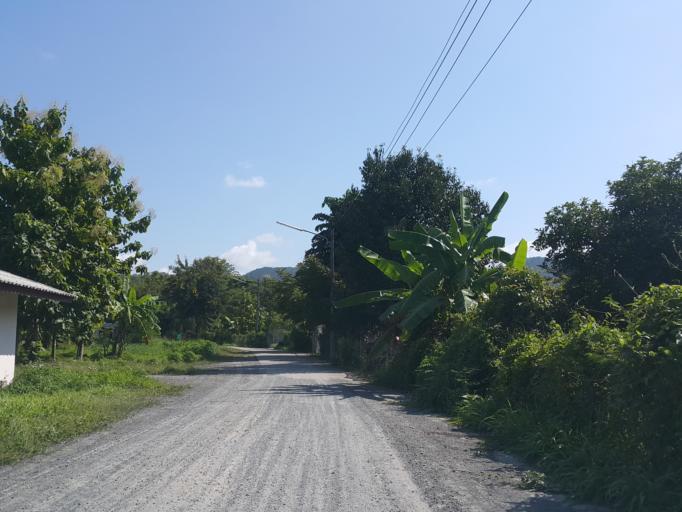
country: TH
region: Chiang Mai
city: Mae On
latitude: 18.8065
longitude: 99.1810
